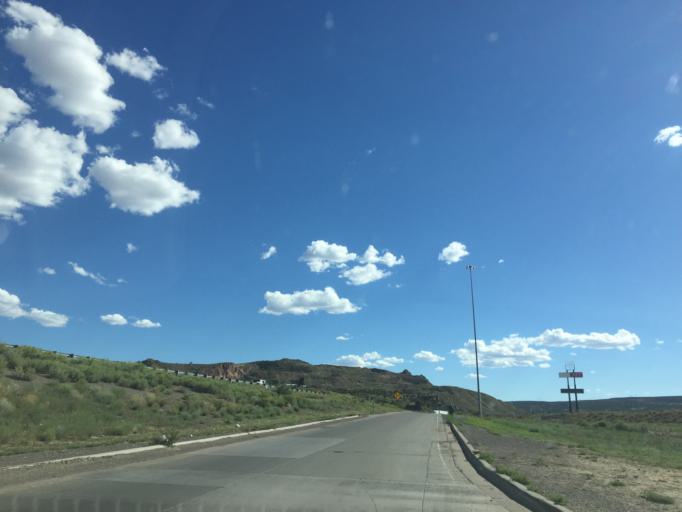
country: US
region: New Mexico
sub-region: McKinley County
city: Gallup
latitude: 35.5048
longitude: -108.8323
